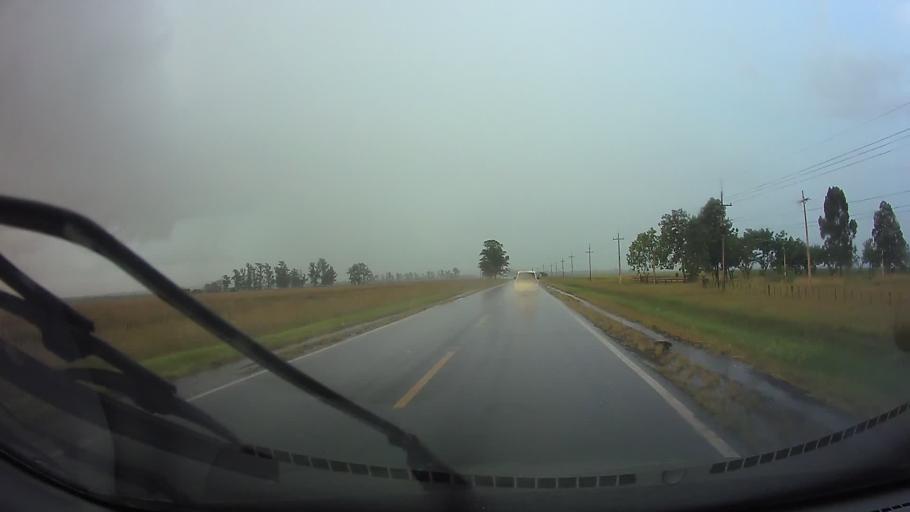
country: PY
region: Paraguari
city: Paraguari
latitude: -25.6616
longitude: -57.1620
